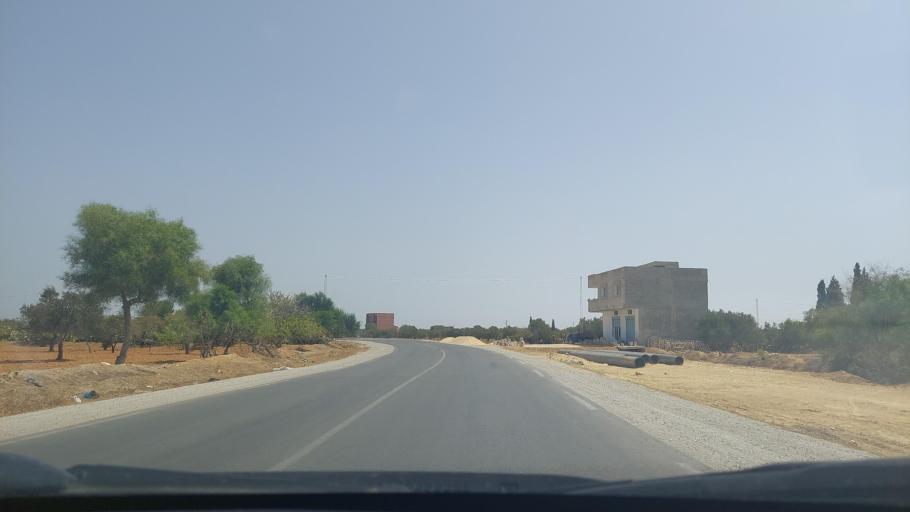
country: TN
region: Al Munastir
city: Qasr Hallal
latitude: 35.6026
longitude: 10.8950
